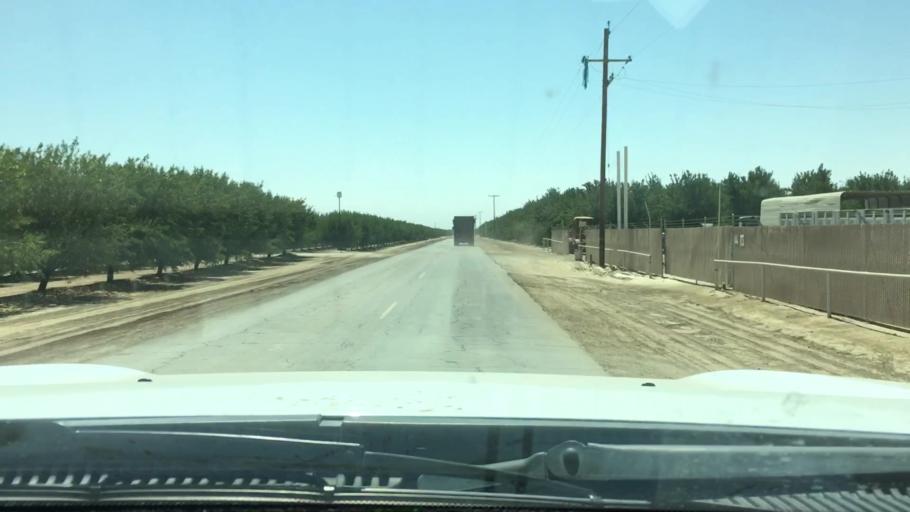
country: US
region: California
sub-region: Kern County
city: Wasco
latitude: 35.5227
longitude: -119.4032
